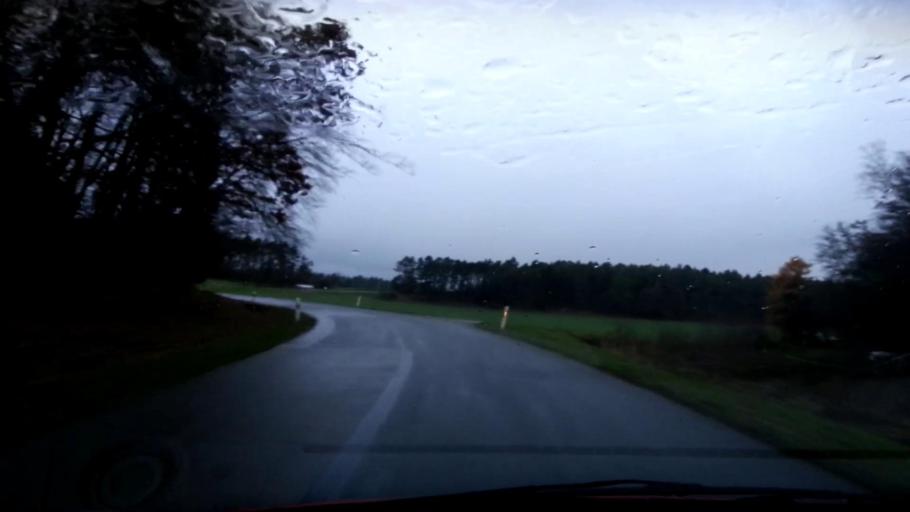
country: DE
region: Bavaria
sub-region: Upper Franconia
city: Aufsess
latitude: 49.9330
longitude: 11.2050
